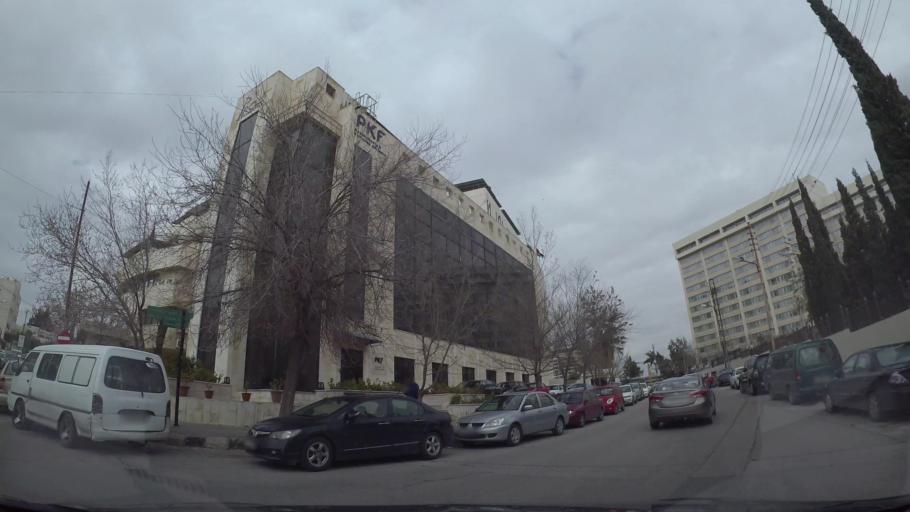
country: JO
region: Amman
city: Amman
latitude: 31.9729
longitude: 35.9054
